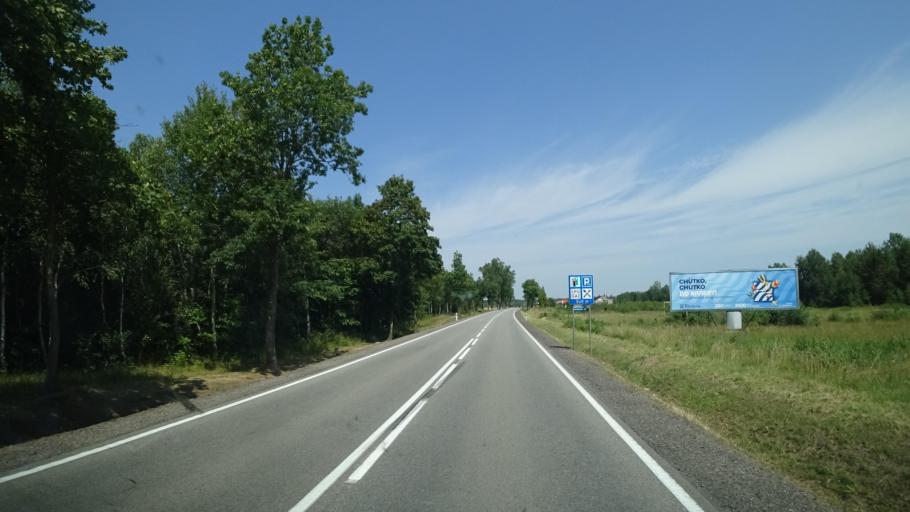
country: PL
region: Pomeranian Voivodeship
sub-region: Powiat koscierski
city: Koscierzyna
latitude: 54.1561
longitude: 18.0328
